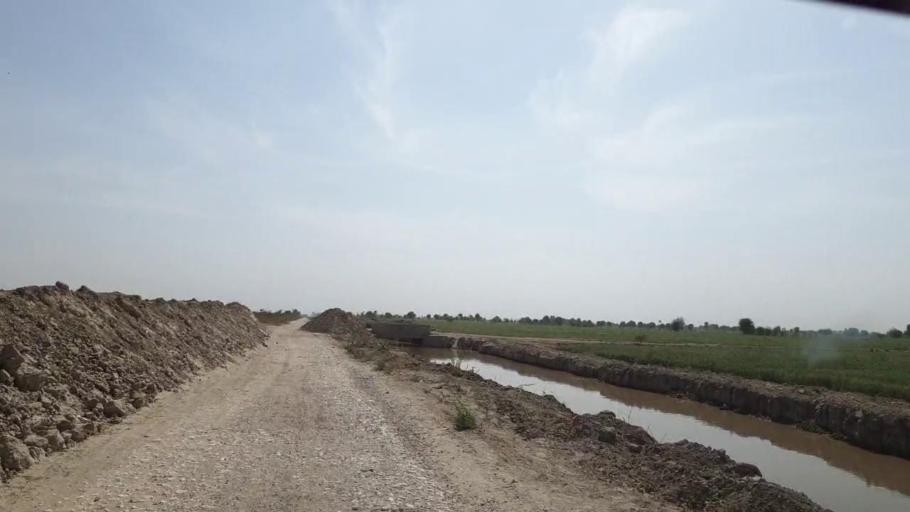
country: PK
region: Sindh
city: Nabisar
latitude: 25.0965
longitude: 69.5819
